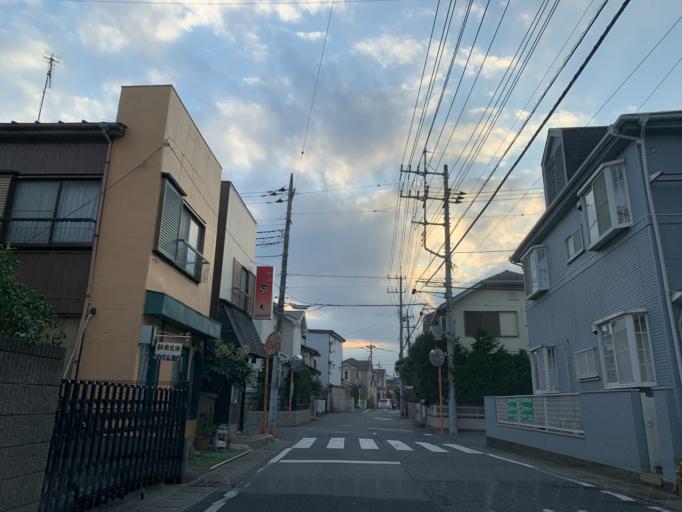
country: JP
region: Chiba
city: Nagareyama
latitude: 35.8940
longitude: 139.9158
